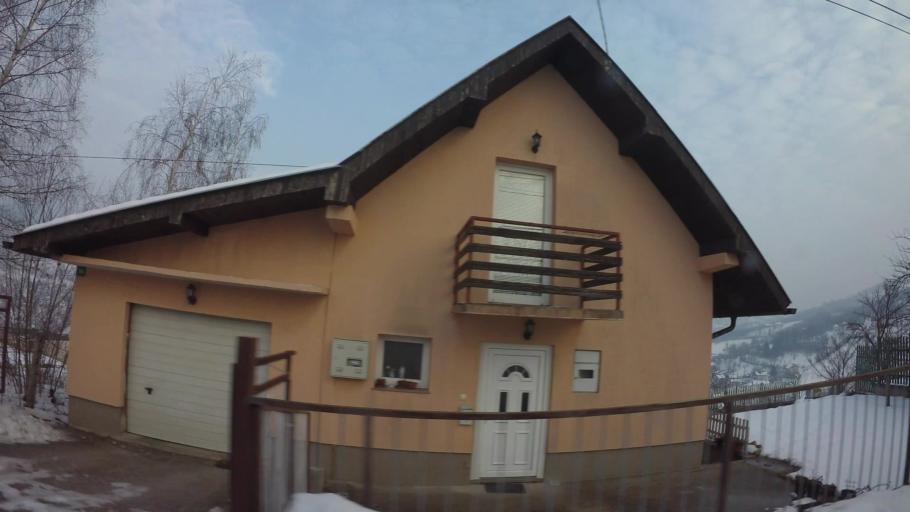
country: BA
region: Federation of Bosnia and Herzegovina
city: Hotonj
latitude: 43.8935
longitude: 18.3681
